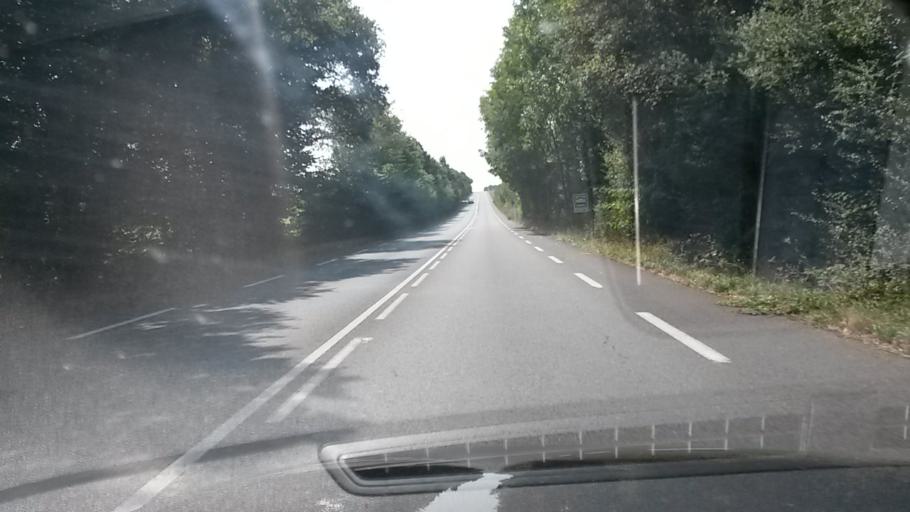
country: FR
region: Pays de la Loire
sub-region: Departement de la Mayenne
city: Saint-Fort
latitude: 47.8146
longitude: -0.7301
